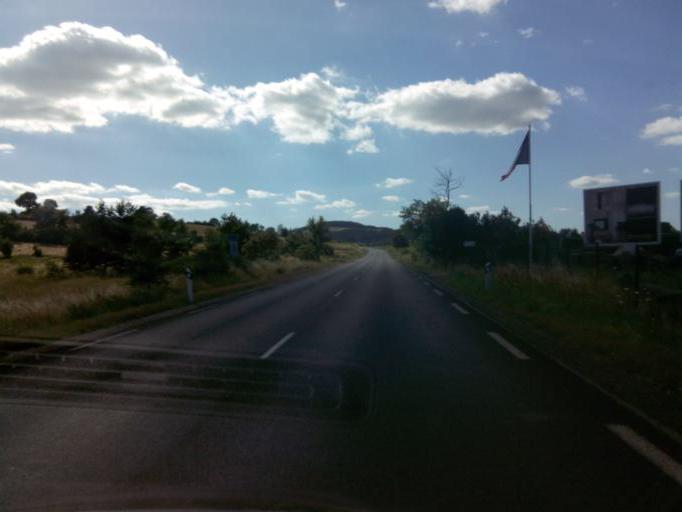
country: FR
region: Auvergne
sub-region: Departement de la Haute-Loire
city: Polignac
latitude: 45.0792
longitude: 3.8323
